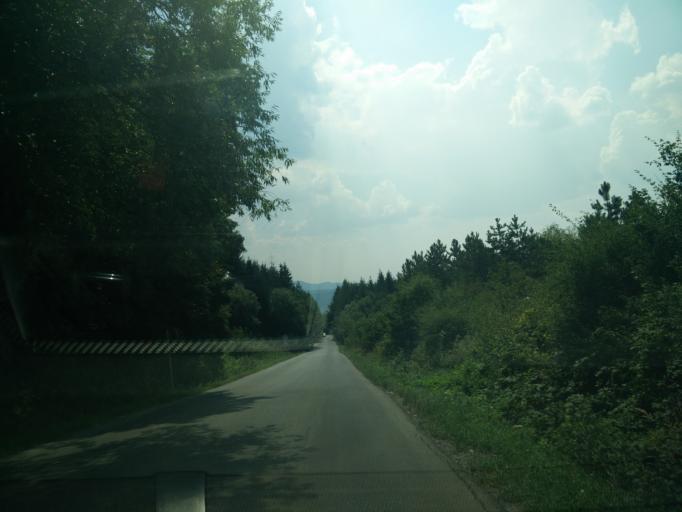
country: SK
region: Banskobystricky
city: Ziar nad Hronom
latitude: 48.5823
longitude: 18.8326
